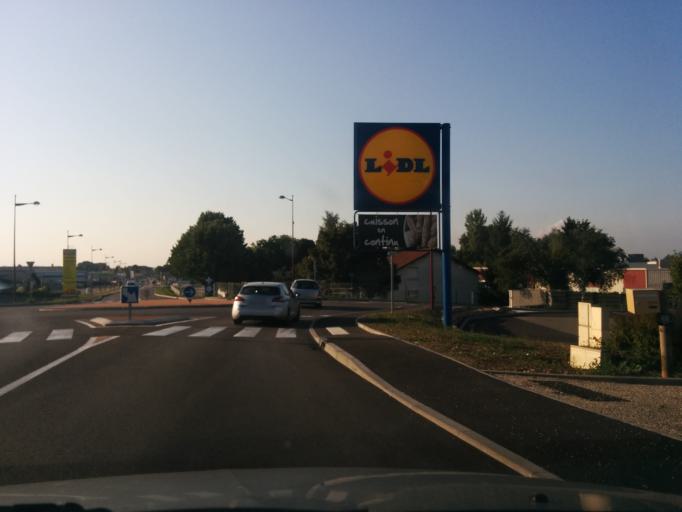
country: FR
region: Rhone-Alpes
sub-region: Departement de l'Isere
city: Les Abrets
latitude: 45.5264
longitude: 5.5925
